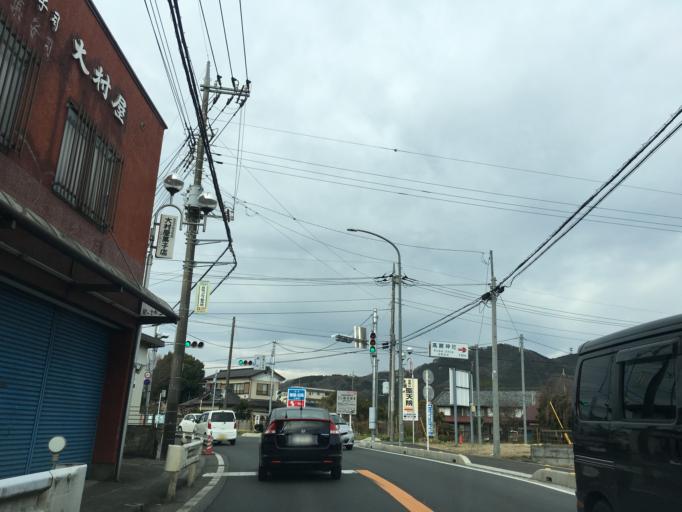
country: JP
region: Saitama
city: Hanno
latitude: 35.8882
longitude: 139.3212
